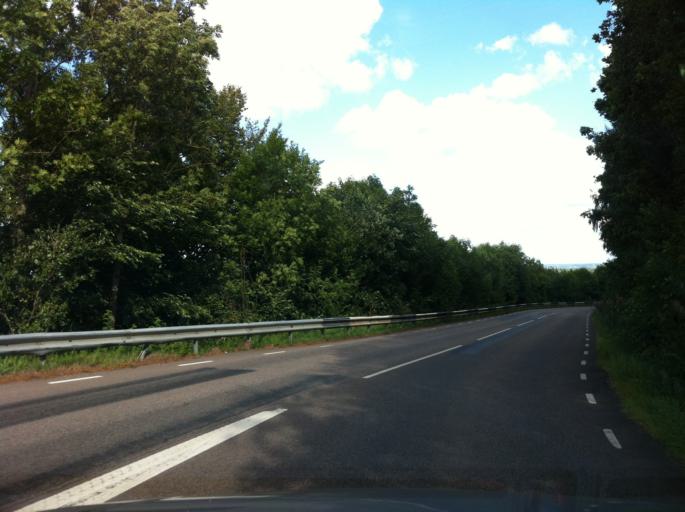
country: SE
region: Skane
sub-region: Bastads Kommun
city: Bastad
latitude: 56.4364
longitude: 12.7920
